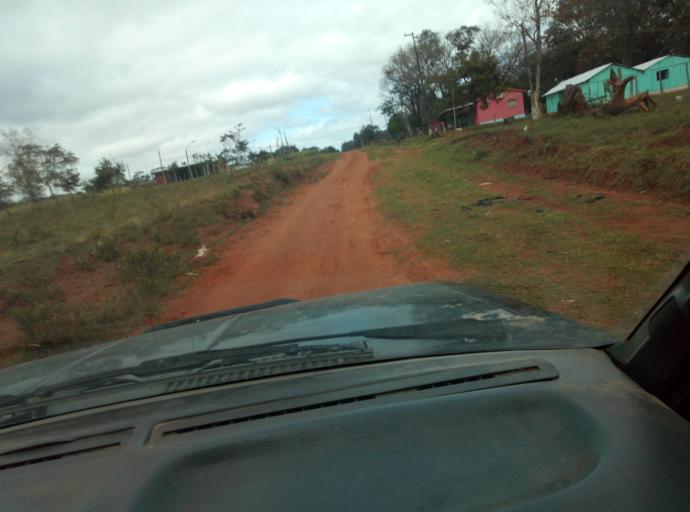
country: PY
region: Caaguazu
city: Doctor Cecilio Baez
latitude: -25.1488
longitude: -56.2906
